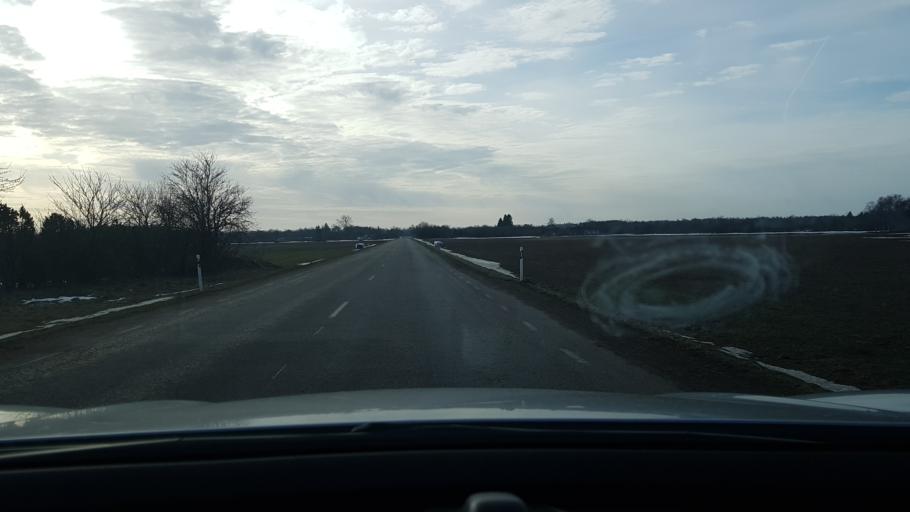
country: EE
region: Saare
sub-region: Kuressaare linn
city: Kuressaare
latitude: 58.3161
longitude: 22.5451
